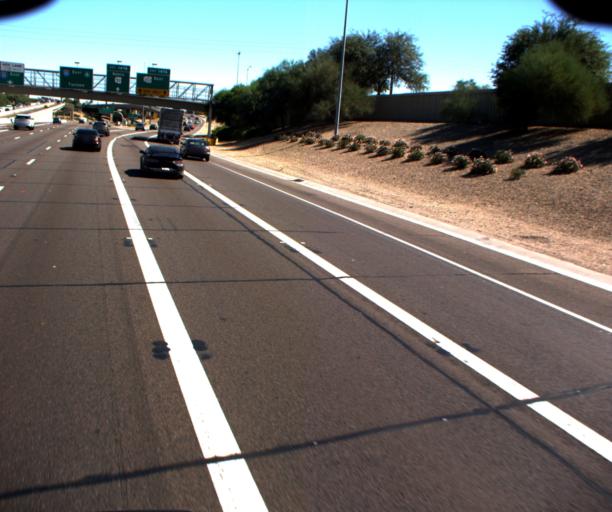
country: US
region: Arizona
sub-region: Maricopa County
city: Phoenix
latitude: 33.4618
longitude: -112.0447
